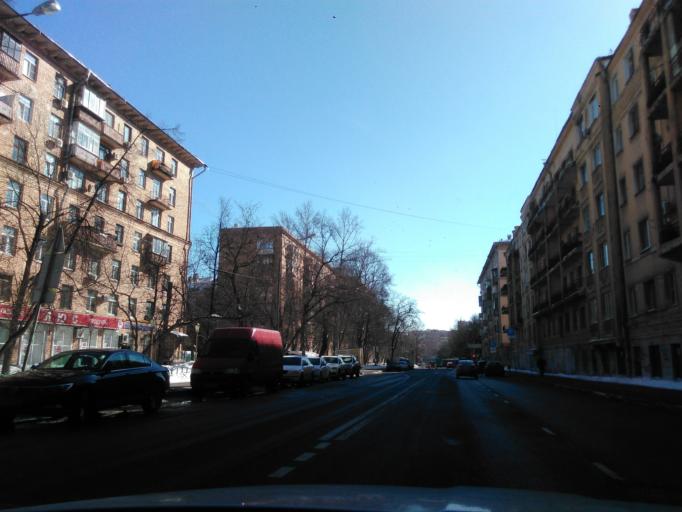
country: RU
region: Moscow
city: Sokol
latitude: 55.7971
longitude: 37.5593
